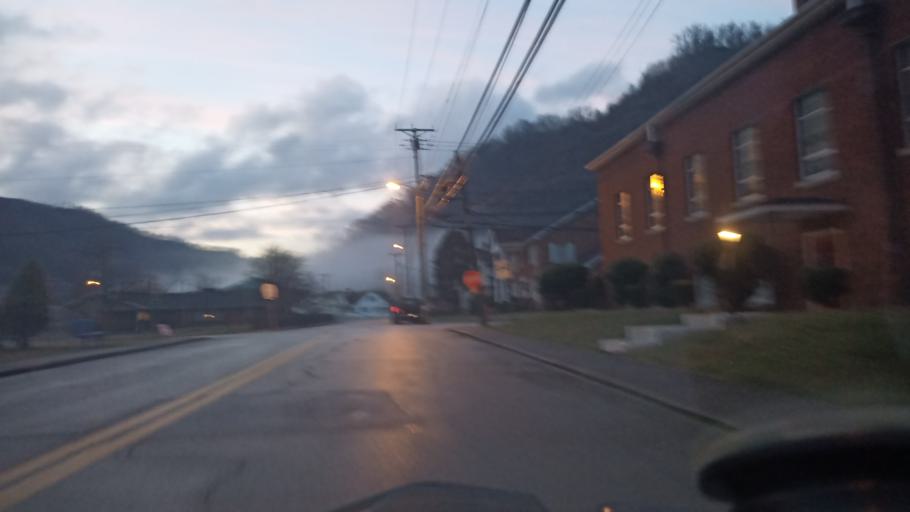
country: US
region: West Virginia
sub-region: Logan County
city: Mallory
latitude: 37.7395
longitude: -81.8775
